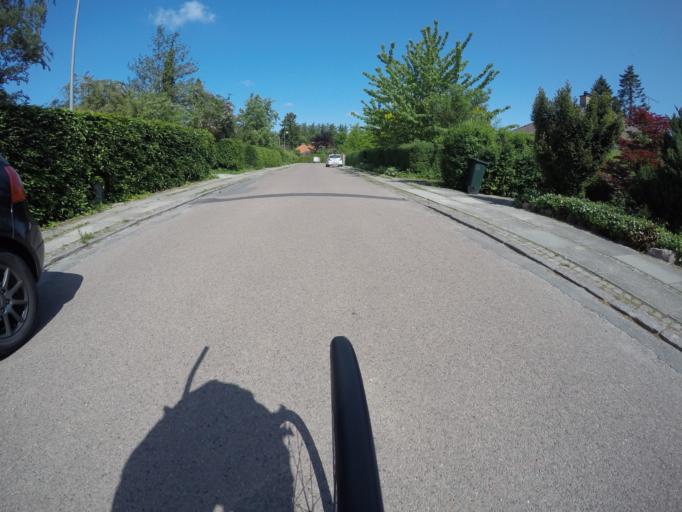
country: DK
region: Capital Region
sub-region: Rudersdal Kommune
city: Holte
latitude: 55.7995
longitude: 12.4682
